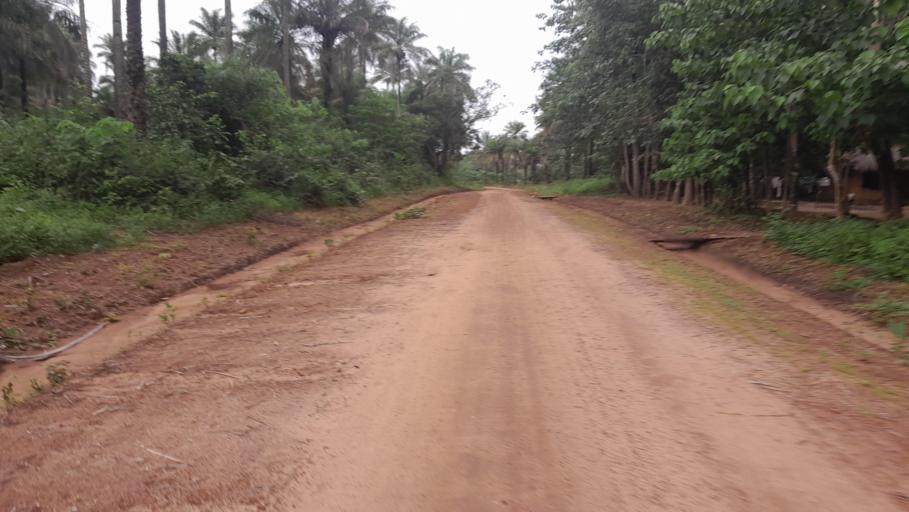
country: GN
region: Boke
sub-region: Boffa
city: Boffa
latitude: 10.0476
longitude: -13.8732
